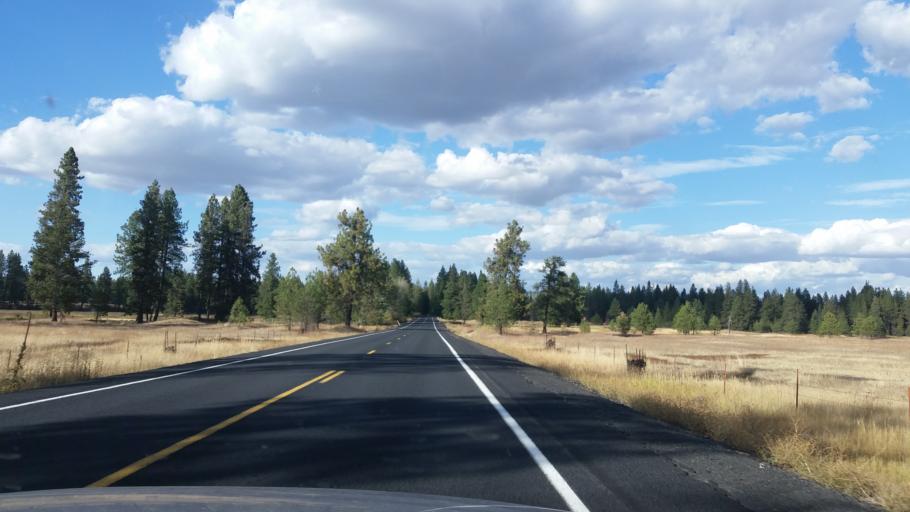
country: US
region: Washington
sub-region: Spokane County
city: Cheney
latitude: 47.3954
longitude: -117.5747
